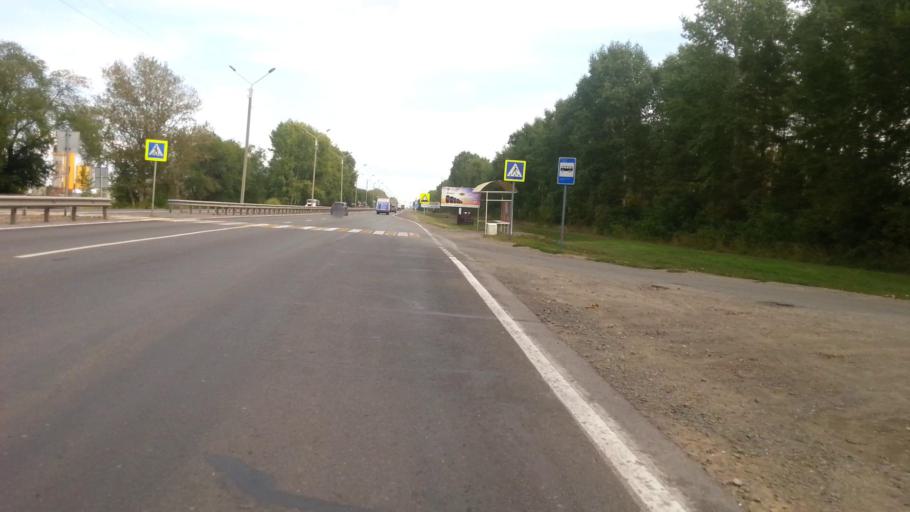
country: RU
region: Altai Krai
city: Vlasikha
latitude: 53.3533
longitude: 83.5576
